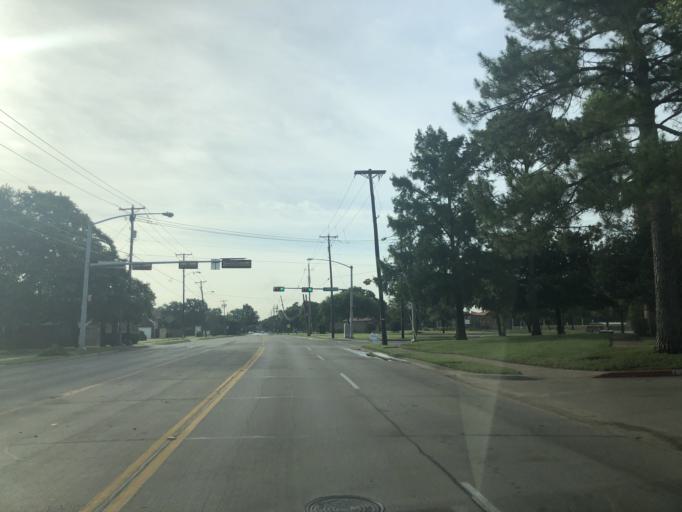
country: US
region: Texas
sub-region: Dallas County
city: Irving
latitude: 32.8023
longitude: -96.9867
